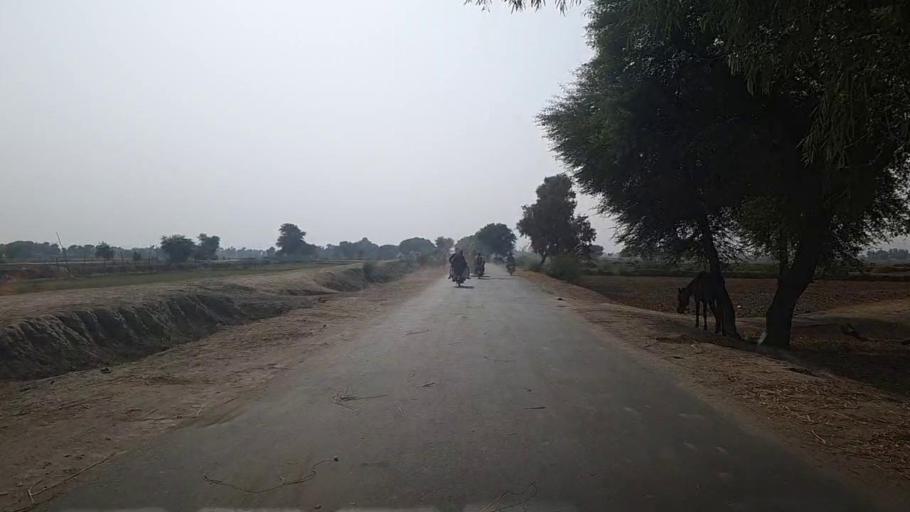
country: PK
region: Sindh
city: Kashmor
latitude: 28.4089
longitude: 69.5618
